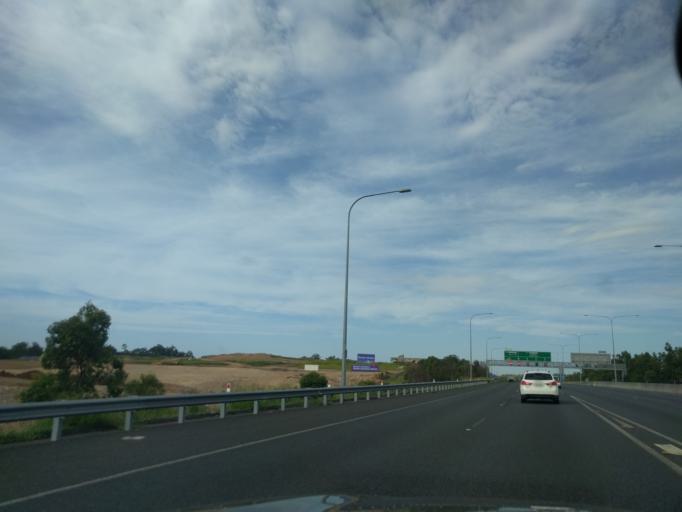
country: AU
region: Queensland
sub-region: Brisbane
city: Wacol
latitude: -27.5807
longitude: 152.9366
